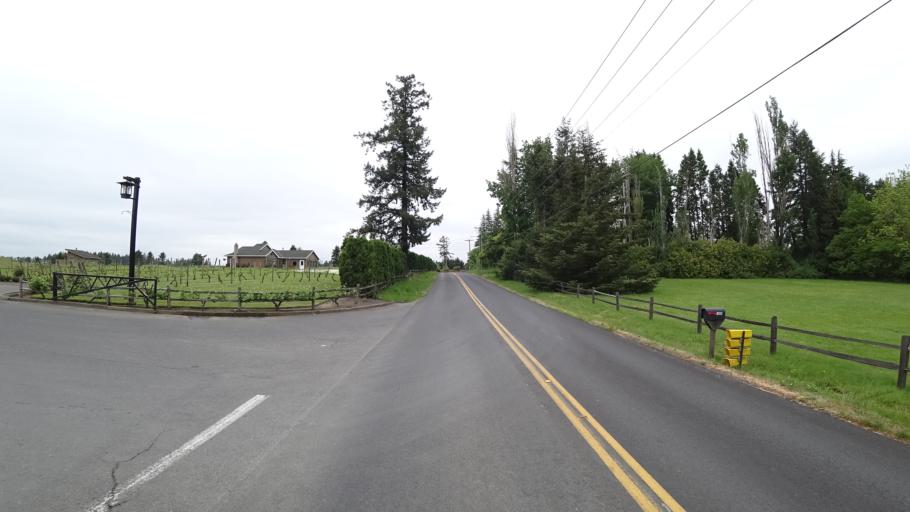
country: US
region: Oregon
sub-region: Washington County
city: Aloha
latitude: 45.4850
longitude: -122.9137
